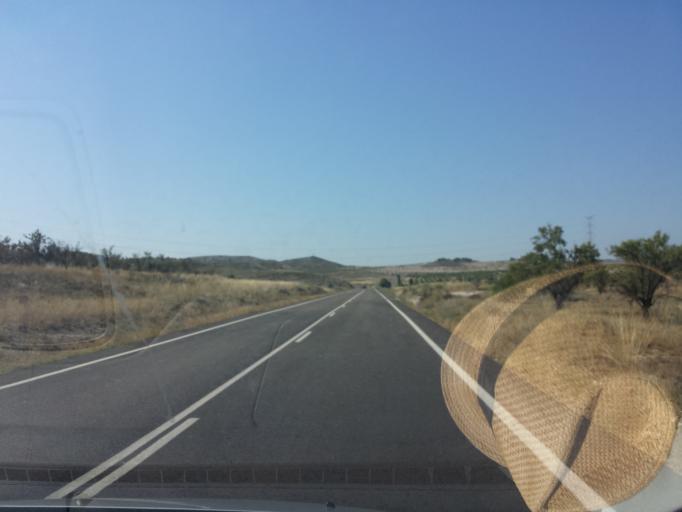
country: ES
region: Aragon
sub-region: Provincia de Zaragoza
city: Paracuellos de Jiloca
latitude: 41.3007
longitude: -1.6779
